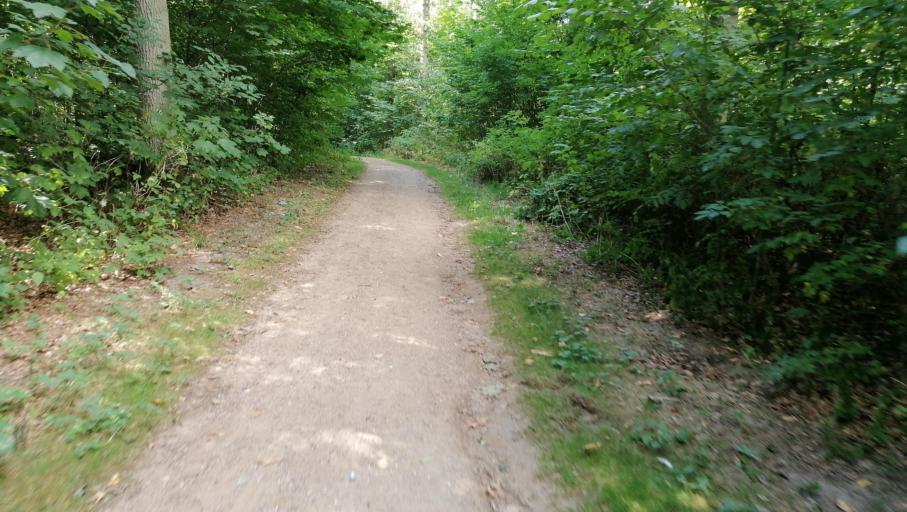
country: DK
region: Zealand
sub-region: Holbaek Kommune
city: Holbaek
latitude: 55.7126
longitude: 11.6892
